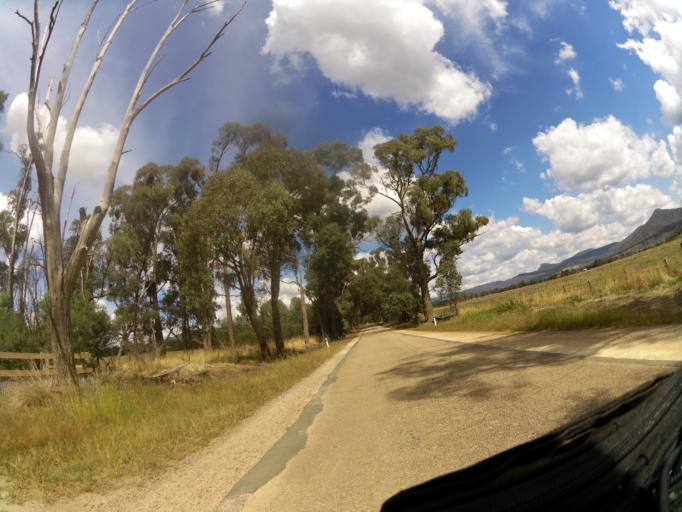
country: AU
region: Victoria
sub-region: Benalla
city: Benalla
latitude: -36.7682
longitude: 145.9756
